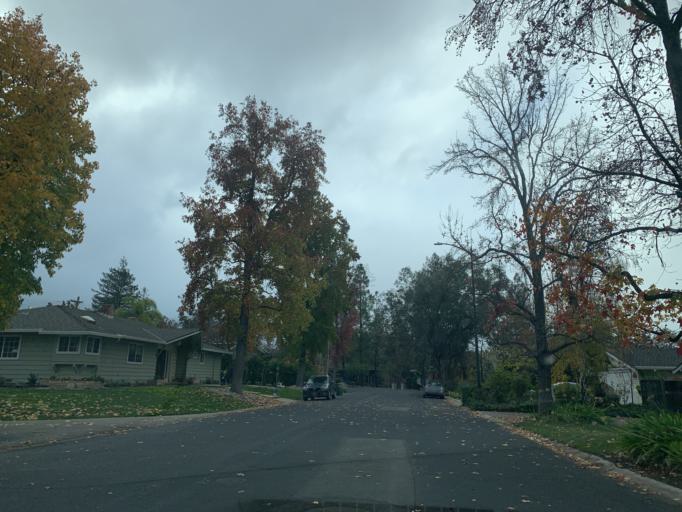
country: US
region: California
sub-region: Santa Clara County
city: Monte Sereno
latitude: 37.2522
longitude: -121.9922
